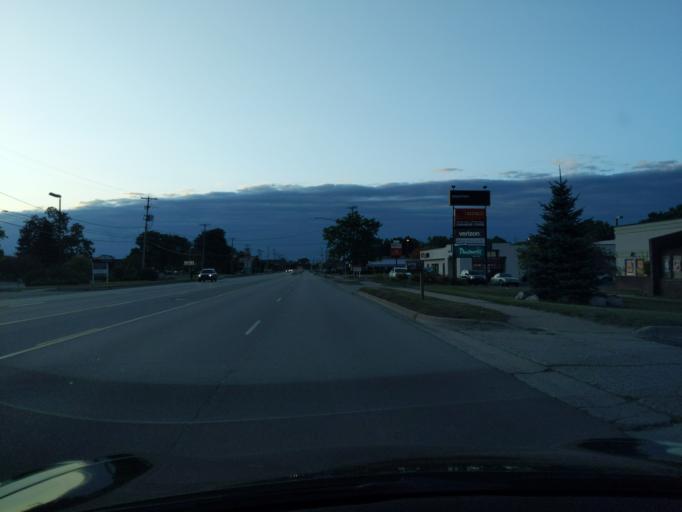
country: US
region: Michigan
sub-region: Ingham County
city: Holt
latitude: 42.6524
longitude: -84.5300
